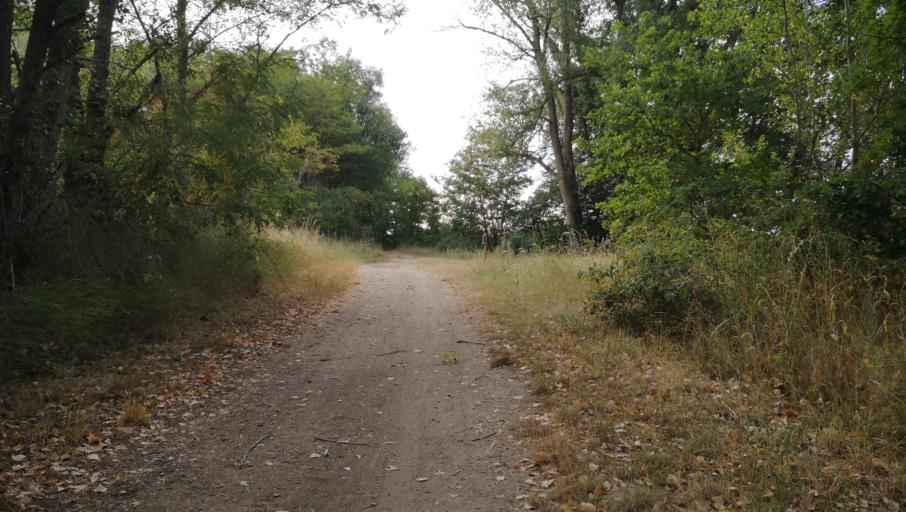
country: FR
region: Centre
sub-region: Departement du Loiret
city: Checy
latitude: 47.8893
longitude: 2.0040
